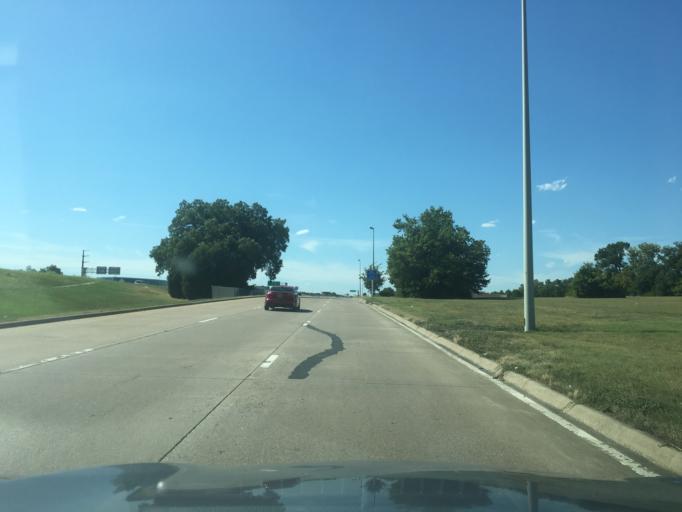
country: US
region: Texas
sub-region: Dallas County
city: Sachse
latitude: 32.9580
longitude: -96.6302
